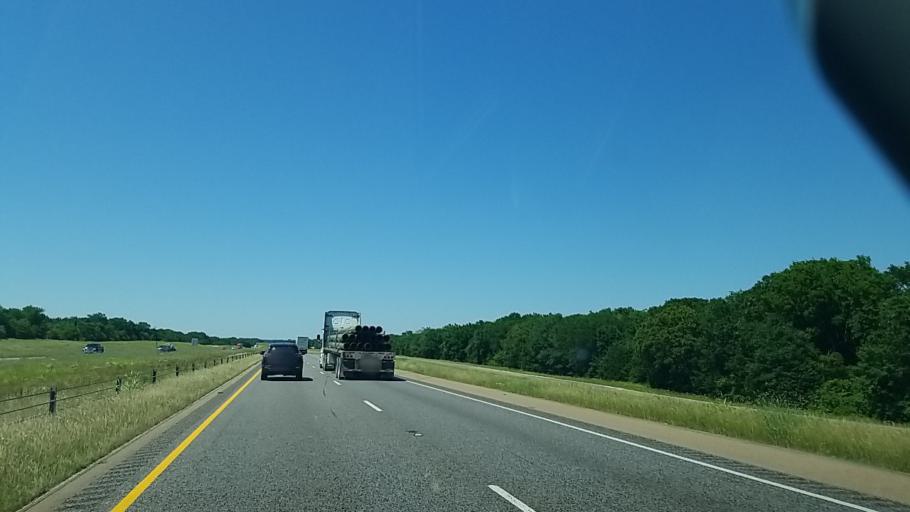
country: US
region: Texas
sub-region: Freestone County
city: Fairfield
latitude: 31.6122
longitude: -96.1566
